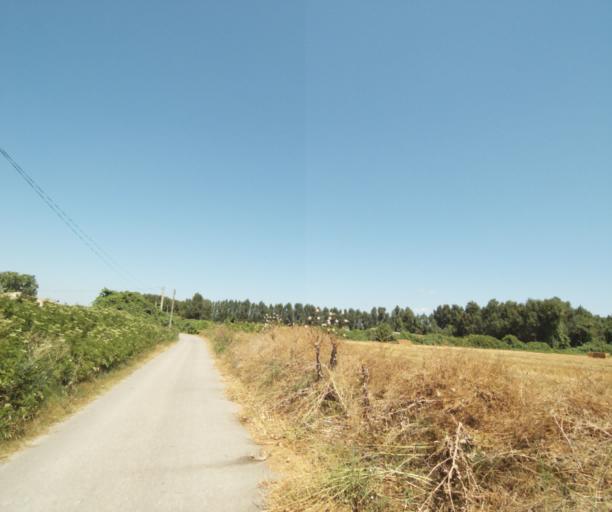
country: FR
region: Languedoc-Roussillon
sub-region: Departement de l'Herault
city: Marsillargues
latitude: 43.6573
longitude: 4.1832
